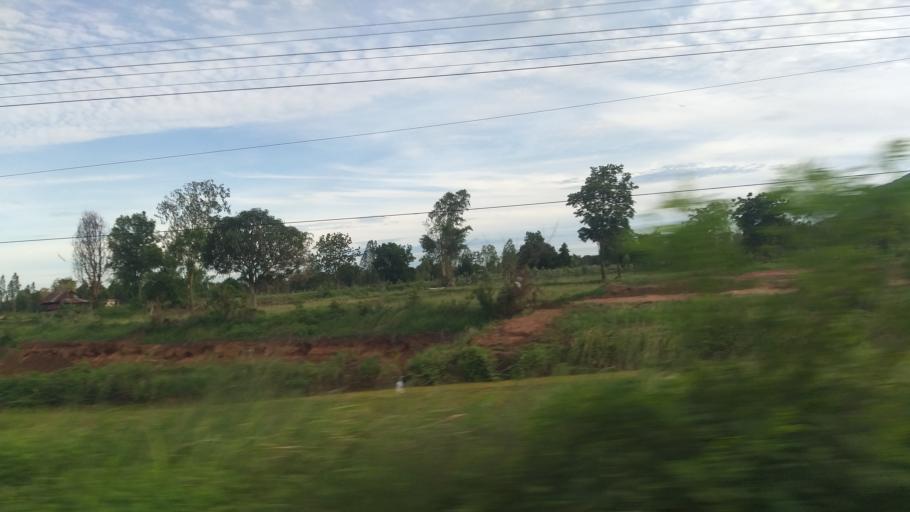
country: TH
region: Chaiyaphum
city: Phu Khiao
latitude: 16.3276
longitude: 102.2152
